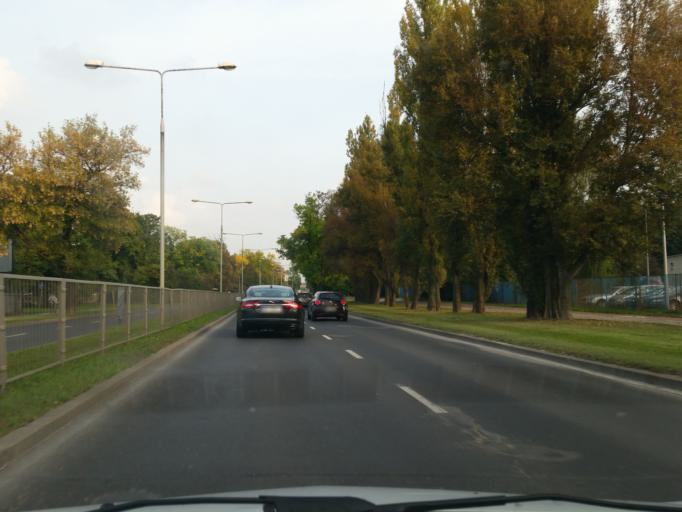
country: PL
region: Masovian Voivodeship
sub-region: Warszawa
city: Wlochy
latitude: 52.1829
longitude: 20.9705
